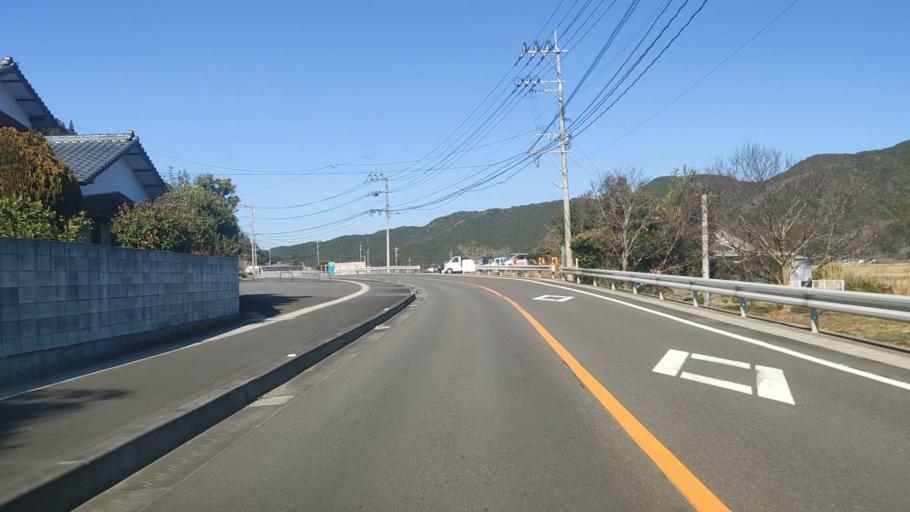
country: JP
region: Oita
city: Saiki
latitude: 32.9269
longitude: 131.9228
